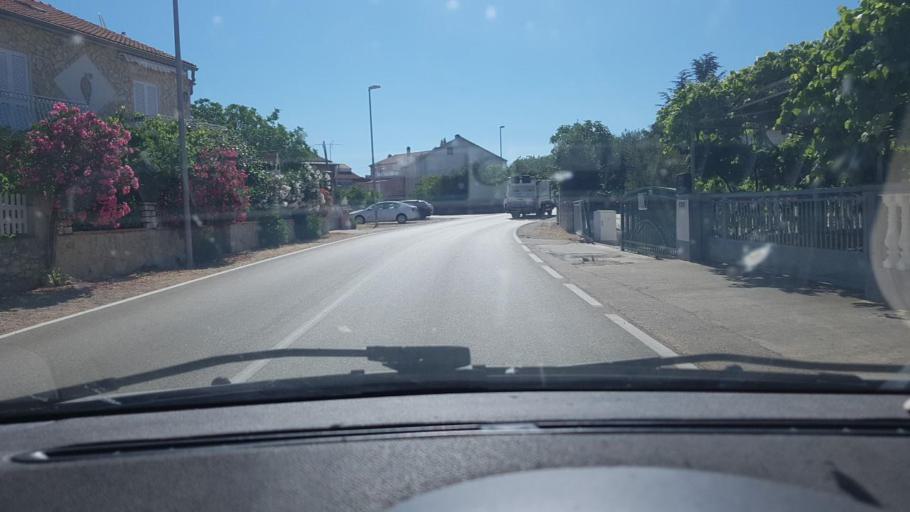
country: HR
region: Sibensko-Kniniska
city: Vodice
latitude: 43.7462
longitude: 15.8057
